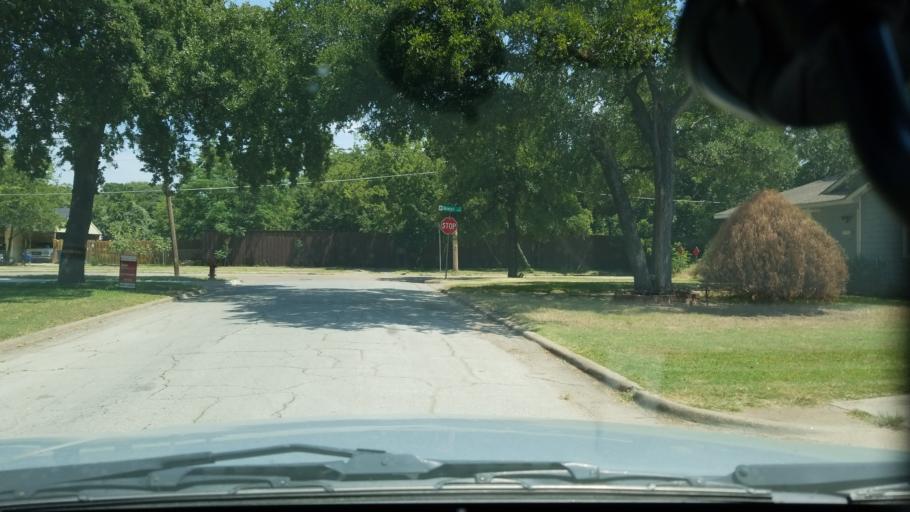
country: US
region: Texas
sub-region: Dallas County
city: Grand Prairie
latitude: 32.7559
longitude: -96.9541
